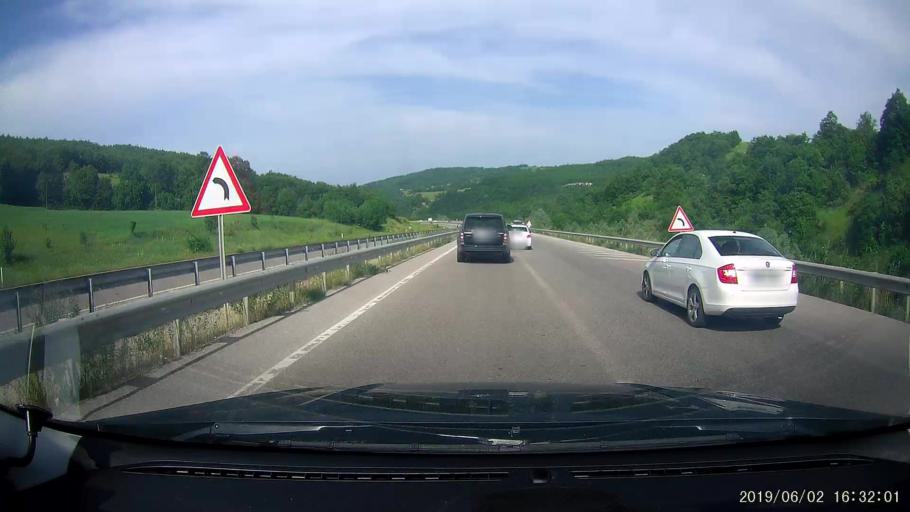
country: TR
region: Samsun
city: Ladik
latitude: 41.0363
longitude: 35.9114
